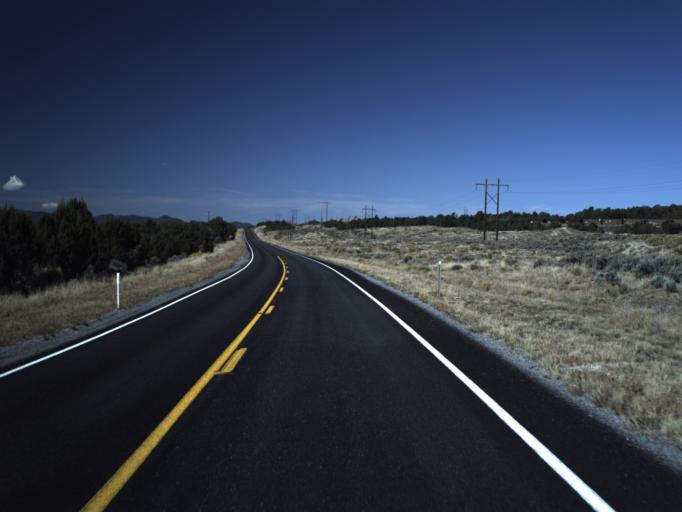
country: US
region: Utah
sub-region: Iron County
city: Cedar City
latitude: 37.6108
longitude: -113.3740
